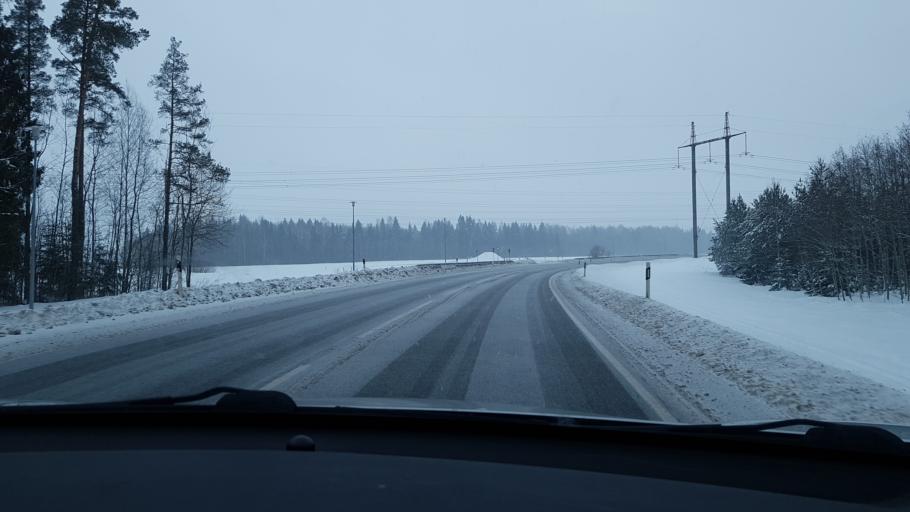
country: EE
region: Jaervamaa
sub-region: Paide linn
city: Paide
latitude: 58.8713
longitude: 25.4952
